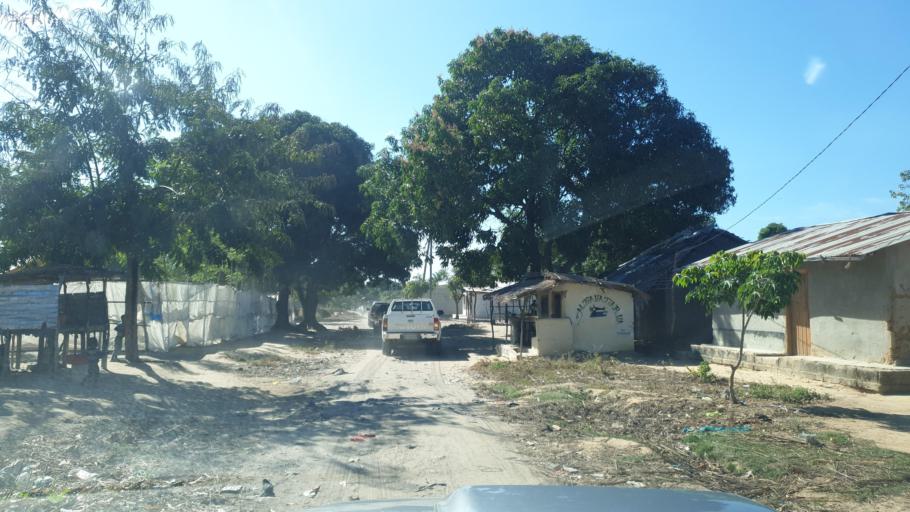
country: MZ
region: Nampula
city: Nacala
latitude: -14.5354
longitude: 40.7030
